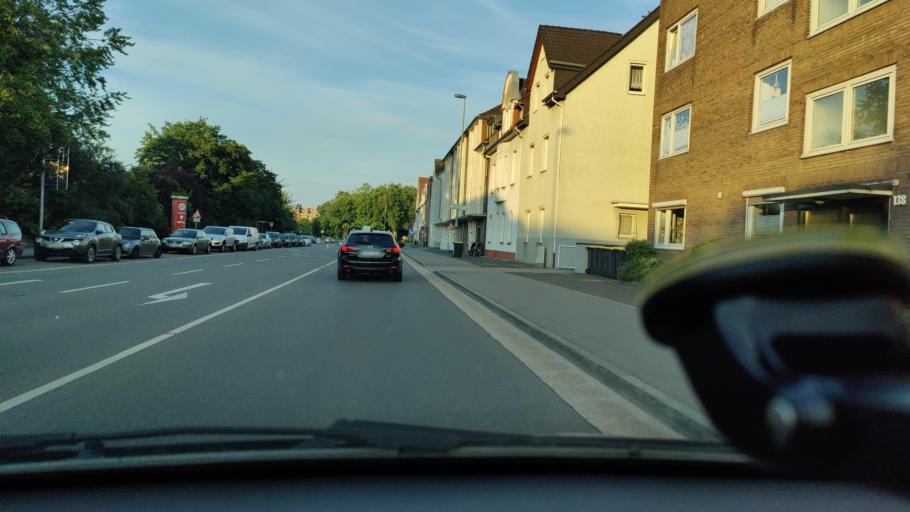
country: DE
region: North Rhine-Westphalia
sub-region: Regierungsbezirk Dusseldorf
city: Kamp-Lintfort
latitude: 51.5037
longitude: 6.5373
